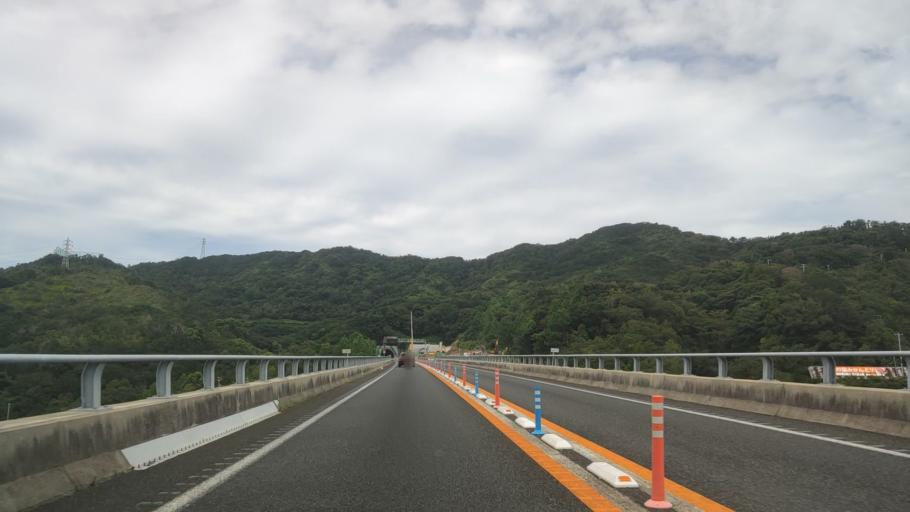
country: JP
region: Wakayama
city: Gobo
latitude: 33.8453
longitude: 135.2184
